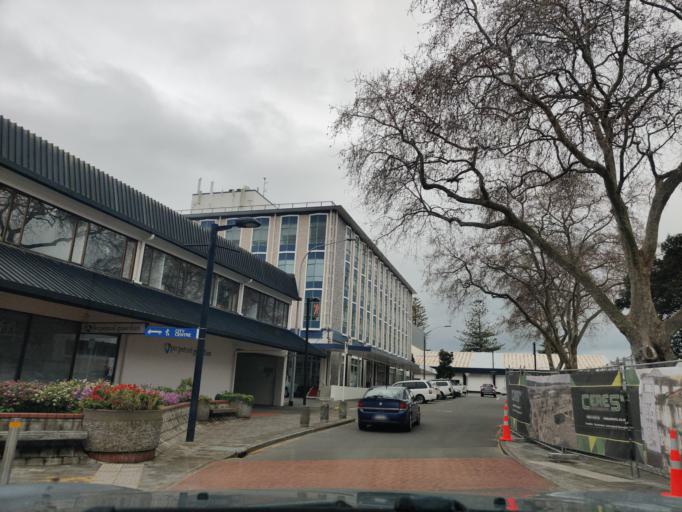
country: NZ
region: Hawke's Bay
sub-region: Napier City
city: Napier
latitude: -39.4924
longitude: 176.9173
